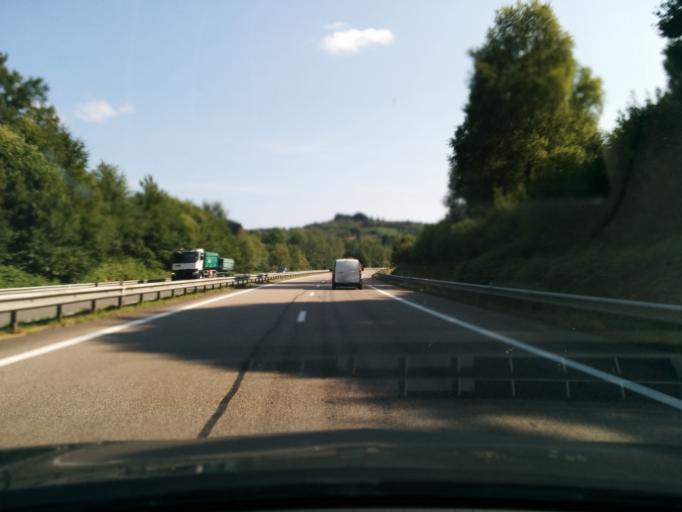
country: FR
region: Limousin
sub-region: Departement de la Haute-Vienne
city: Razes
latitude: 45.9828
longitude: 1.3261
